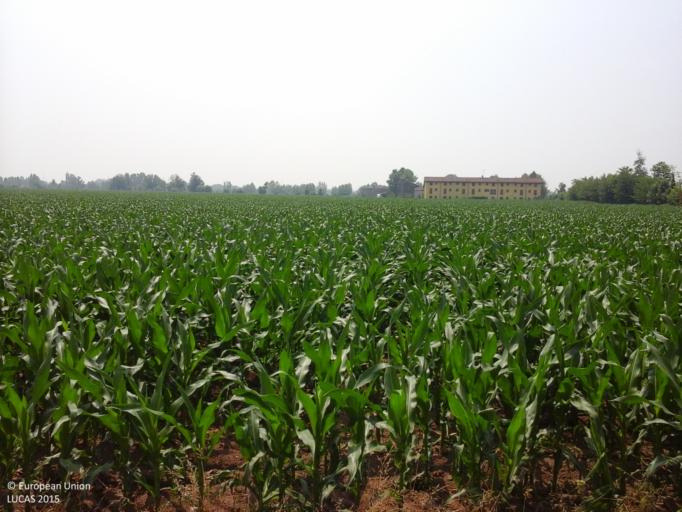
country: IT
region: Lombardy
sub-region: Provincia di Brescia
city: Manerbio
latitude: 45.3606
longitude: 10.1148
